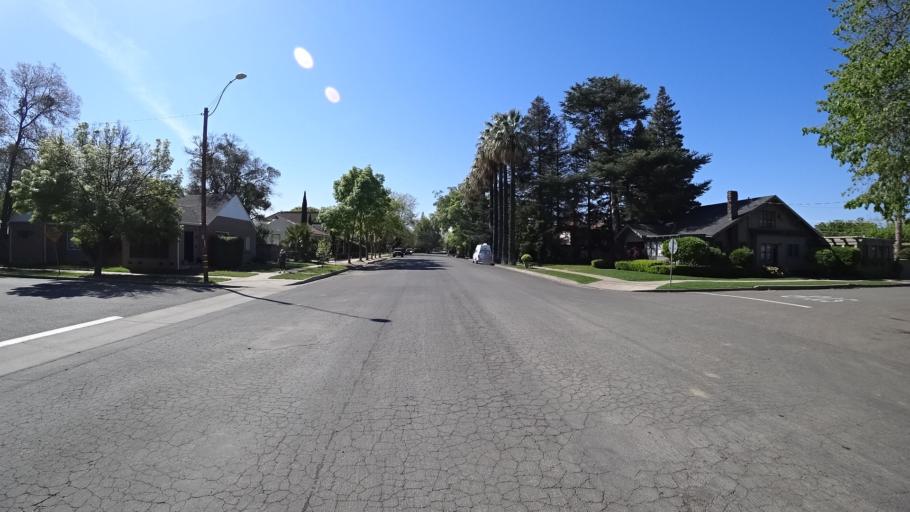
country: US
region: California
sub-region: Glenn County
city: Willows
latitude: 39.5219
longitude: -122.2032
